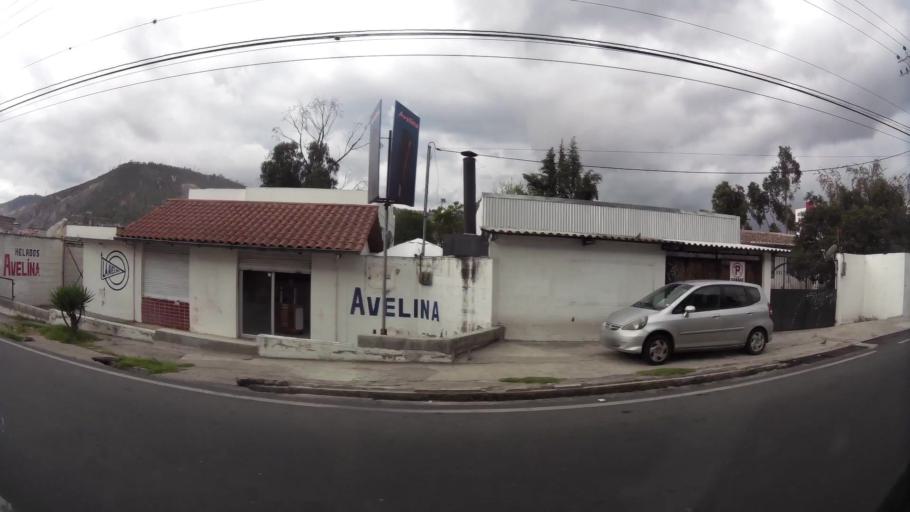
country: EC
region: Pichincha
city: Quito
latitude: -0.0612
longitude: -78.4564
